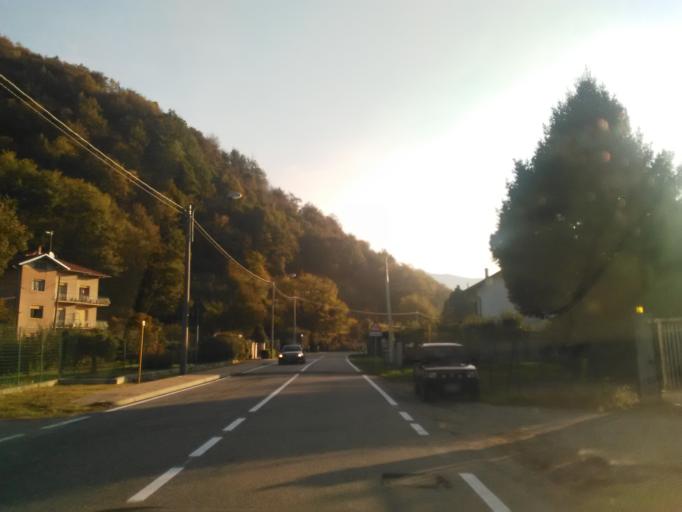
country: IT
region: Piedmont
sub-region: Provincia di Vercelli
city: Borgosesia
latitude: 45.6990
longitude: 8.2727
